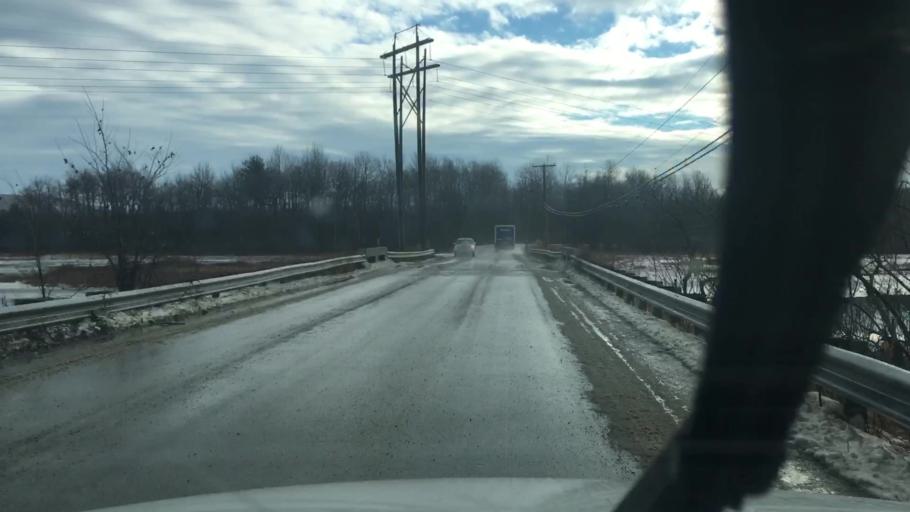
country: US
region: Maine
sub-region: Penobscot County
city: Brewer
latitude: 44.7300
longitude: -68.7572
